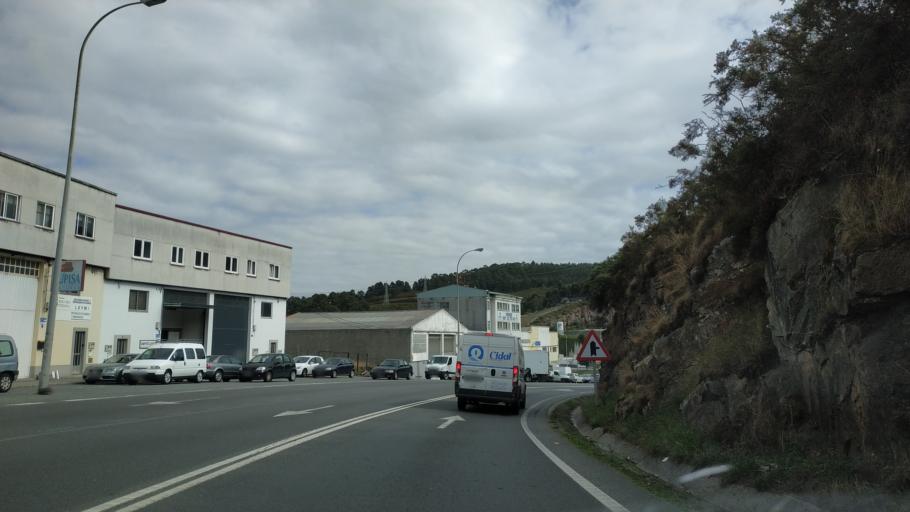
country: ES
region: Galicia
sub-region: Provincia da Coruna
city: A Coruna
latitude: 43.3395
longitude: -8.4484
